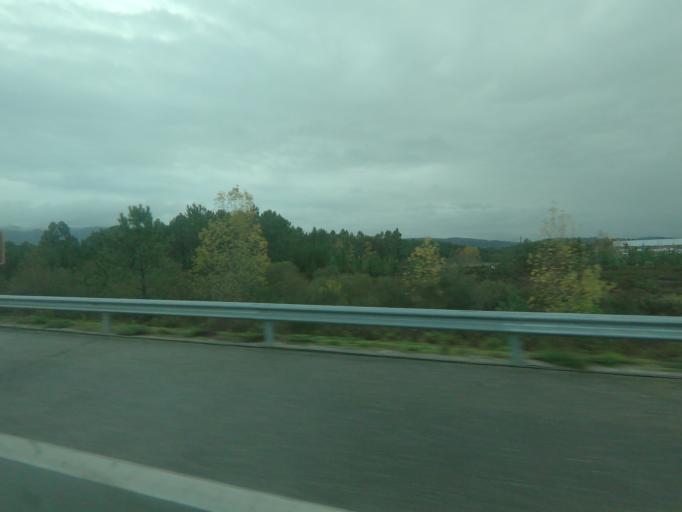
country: PT
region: Viana do Castelo
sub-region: Valenca
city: Valenza
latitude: 41.9724
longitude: -8.6632
